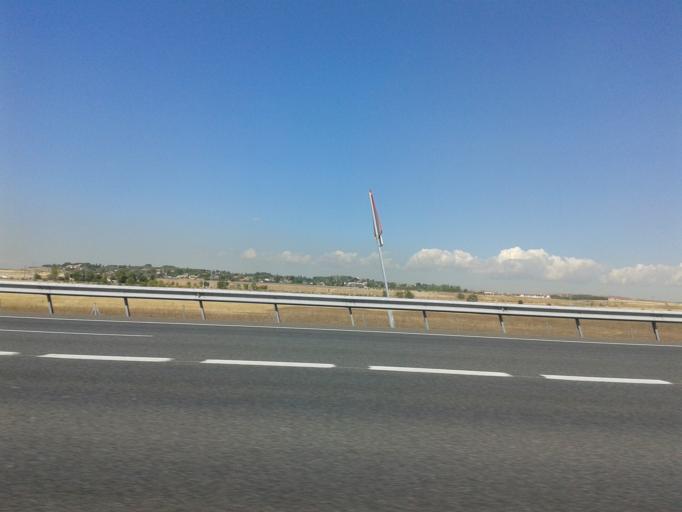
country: ES
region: Madrid
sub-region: Provincia de Madrid
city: Torrejon de Ardoz
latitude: 40.4604
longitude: -3.4987
